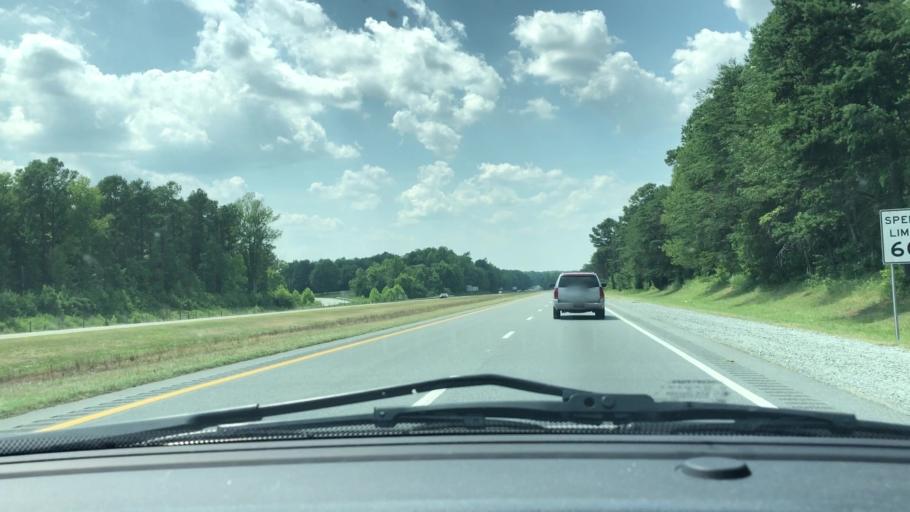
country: US
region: North Carolina
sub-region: Guilford County
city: Forest Oaks
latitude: 35.9694
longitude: -79.7153
